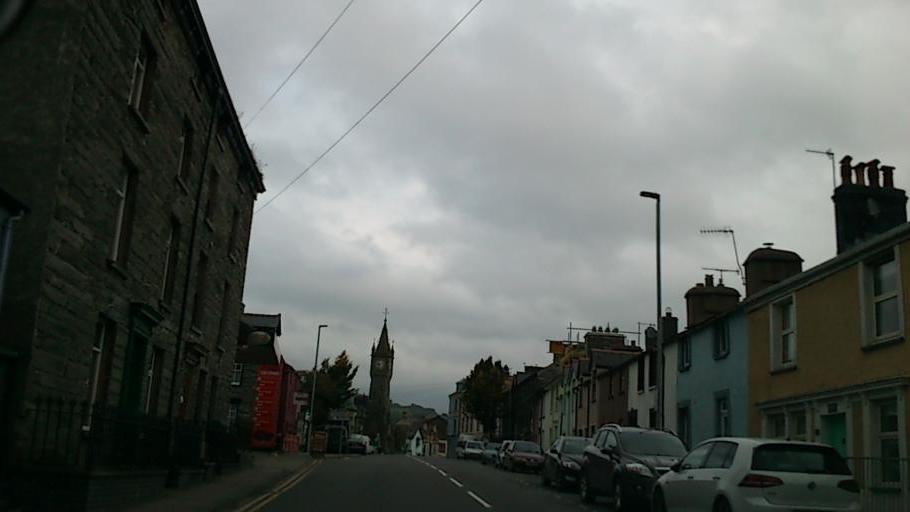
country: GB
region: Wales
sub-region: Sir Powys
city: Machynlleth
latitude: 52.5891
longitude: -3.8531
